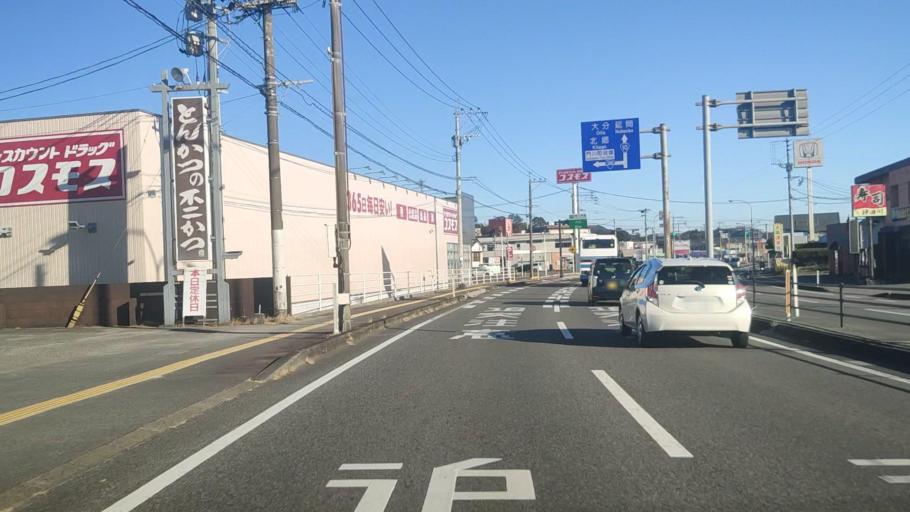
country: JP
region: Miyazaki
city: Nobeoka
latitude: 32.4668
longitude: 131.6480
